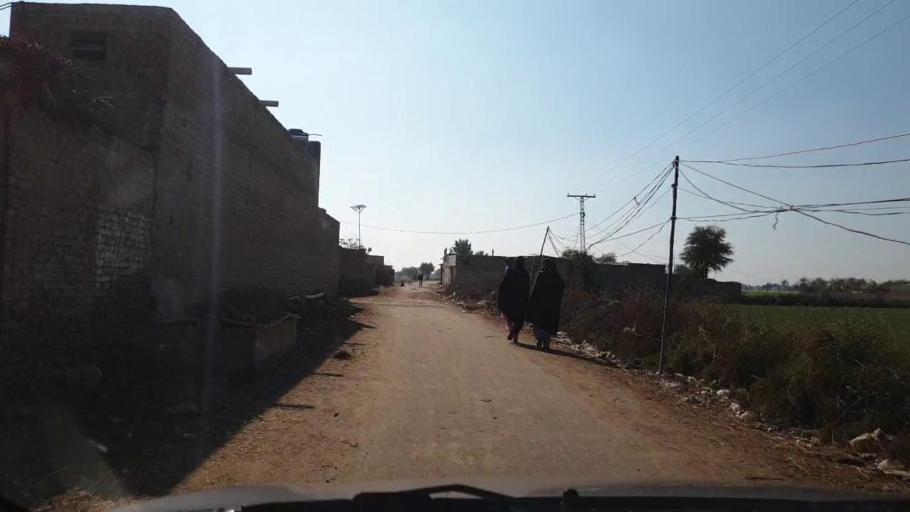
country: PK
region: Sindh
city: Sinjhoro
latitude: 25.9562
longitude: 68.7449
